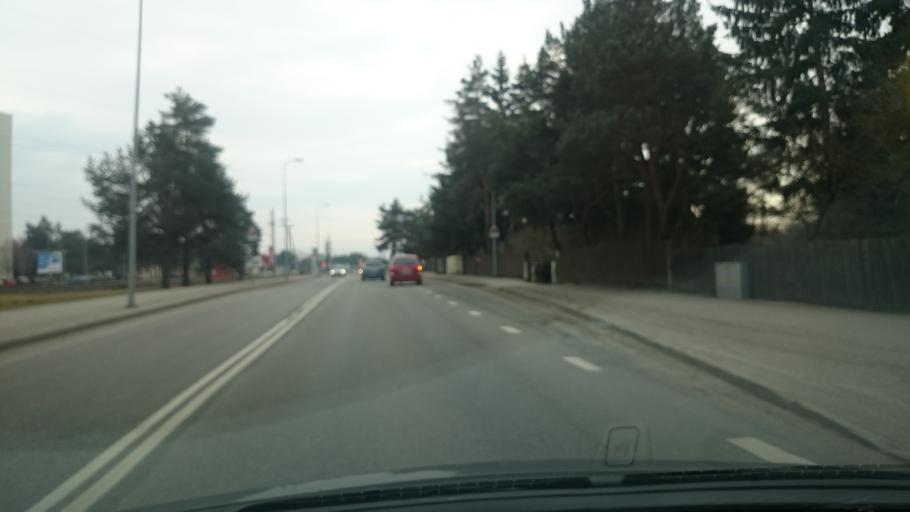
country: EE
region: Harju
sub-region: Saue vald
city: Laagri
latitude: 59.3631
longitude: 24.6290
